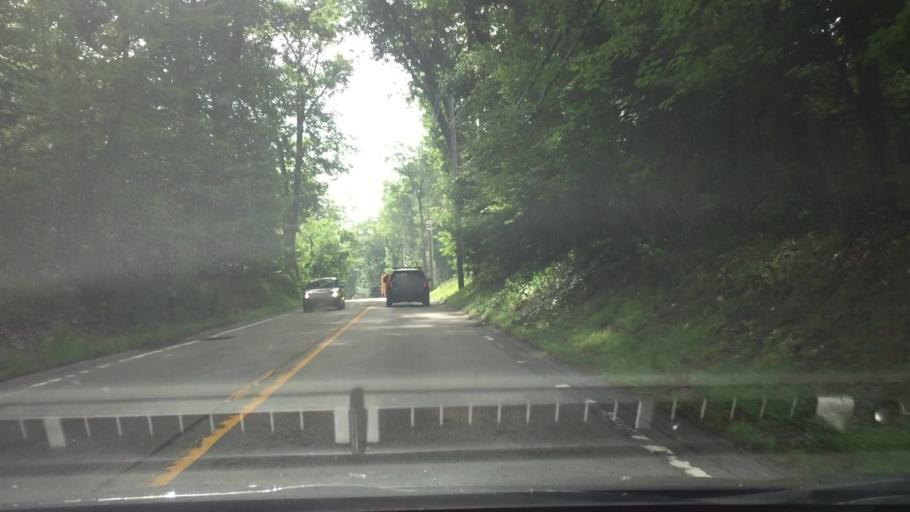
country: US
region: Massachusetts
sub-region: Middlesex County
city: Stow
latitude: 42.4832
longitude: -71.5250
